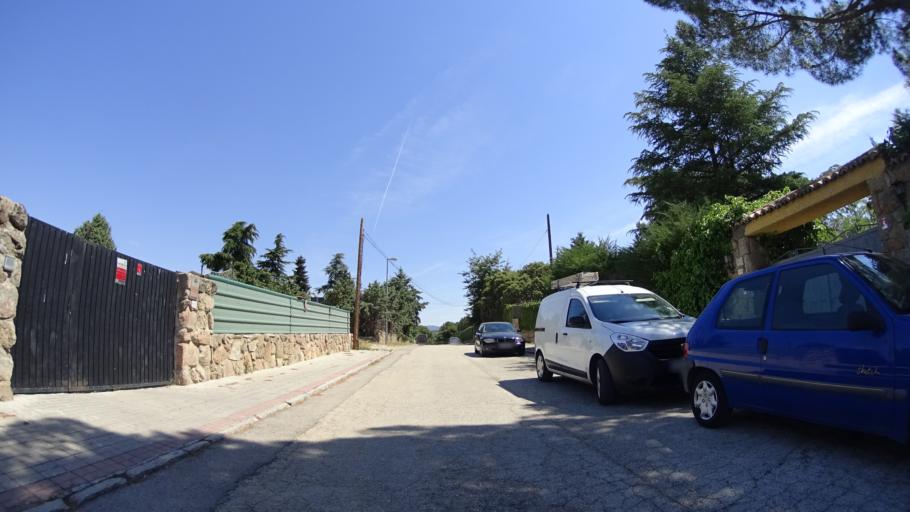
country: ES
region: Madrid
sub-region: Provincia de Madrid
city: Colmenarejo
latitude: 40.5474
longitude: -4.0051
